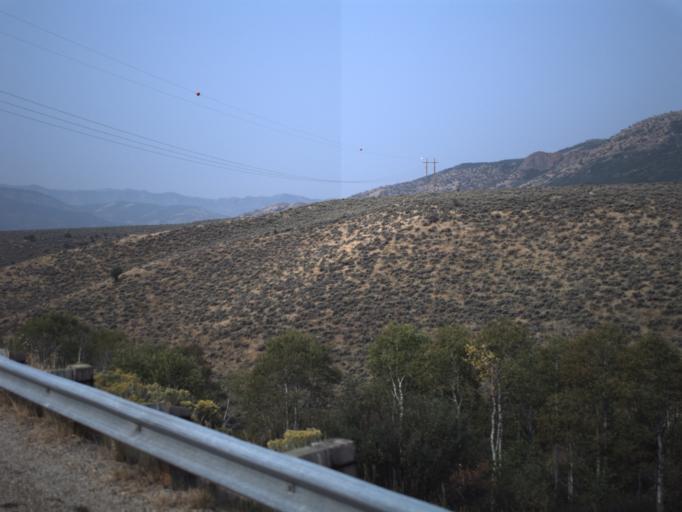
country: US
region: Utah
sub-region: Morgan County
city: Morgan
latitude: 40.9448
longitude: -111.5557
